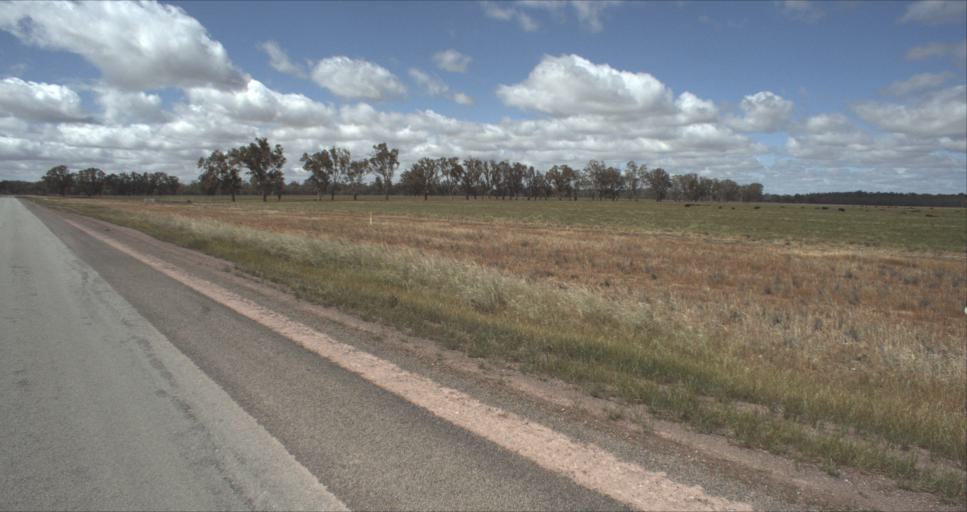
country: AU
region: New South Wales
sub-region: Murrumbidgee Shire
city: Darlington Point
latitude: -34.5717
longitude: 146.0379
